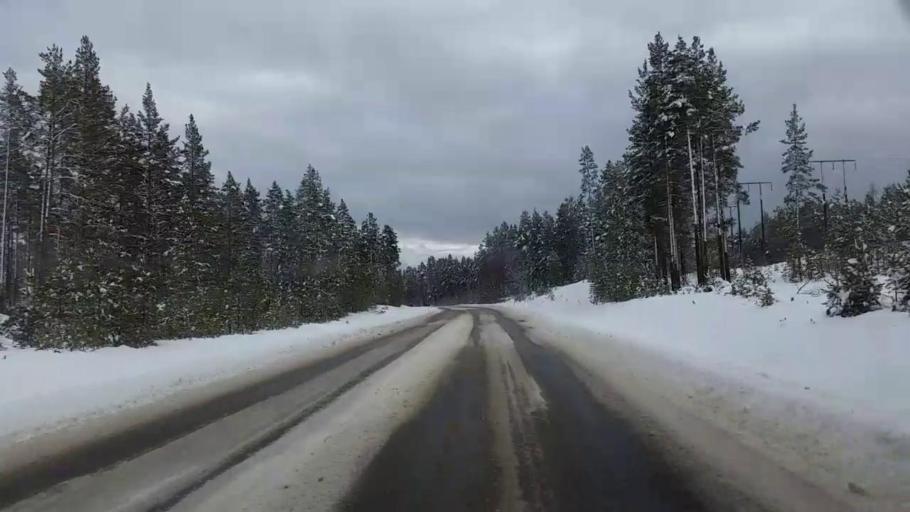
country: SE
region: Vaesternorrland
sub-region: Ange Kommun
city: Ange
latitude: 62.0612
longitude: 15.1144
